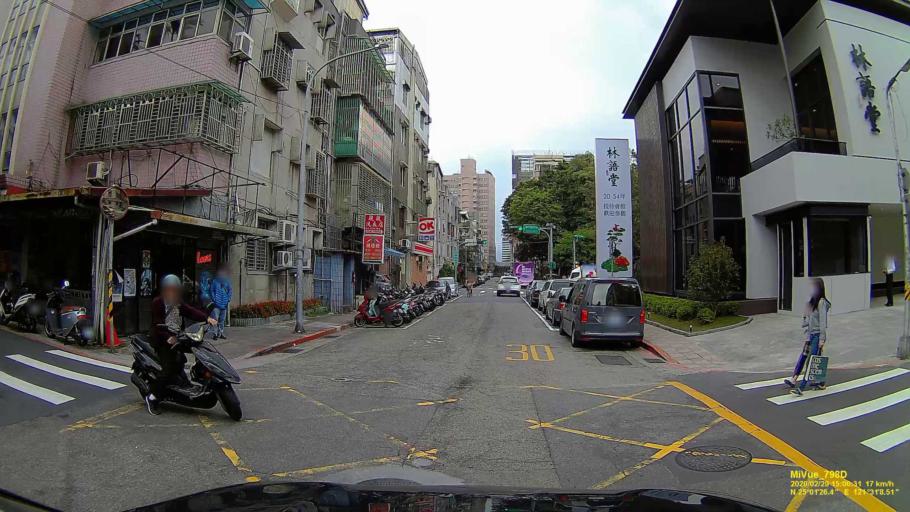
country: TW
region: Taipei
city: Taipei
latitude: 25.0239
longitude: 121.5190
